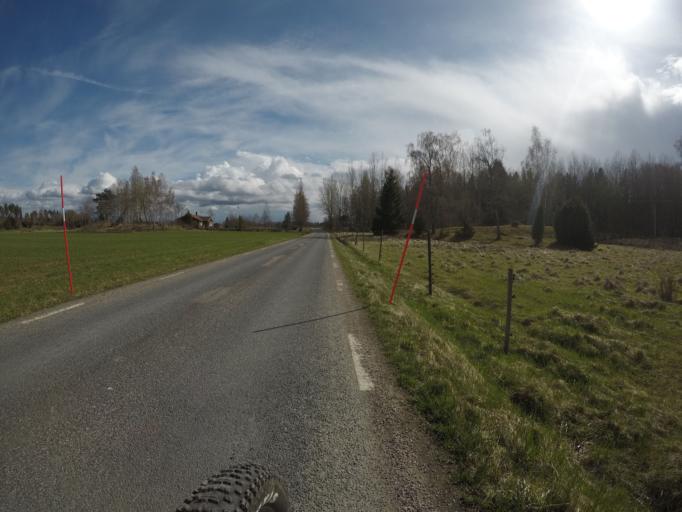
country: SE
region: Vaestmanland
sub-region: Kungsors Kommun
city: Kungsoer
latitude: 59.2958
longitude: 16.1417
